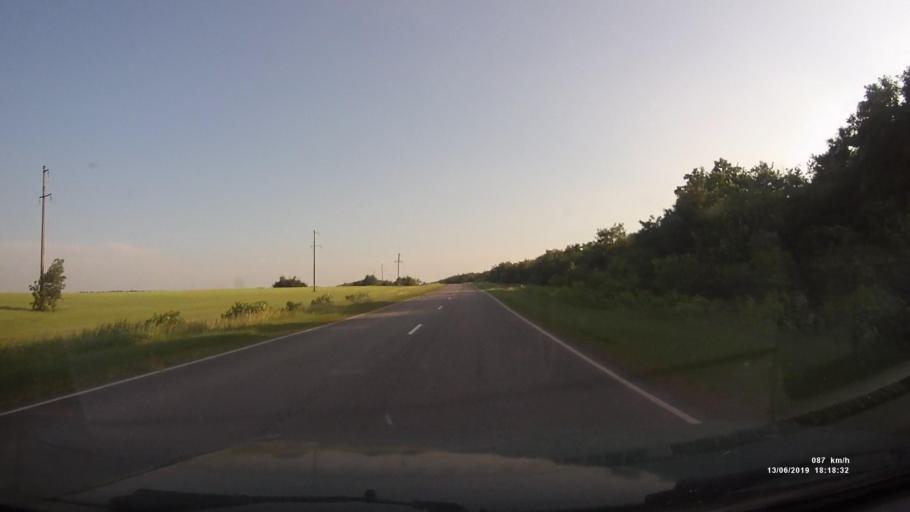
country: RU
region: Rostov
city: Kazanskaya
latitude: 49.9070
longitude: 41.3121
